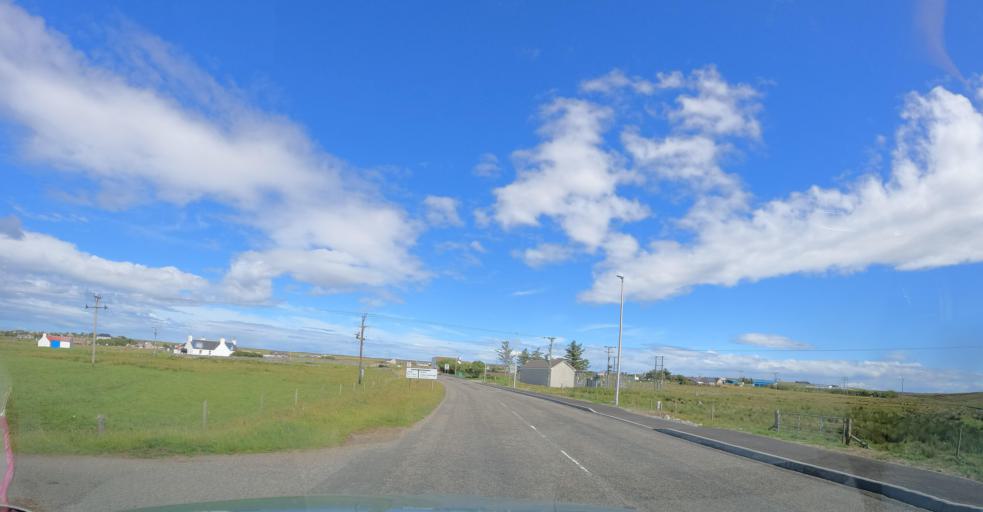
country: GB
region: Scotland
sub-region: Eilean Siar
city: Isle of Lewis
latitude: 58.3490
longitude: -6.5229
